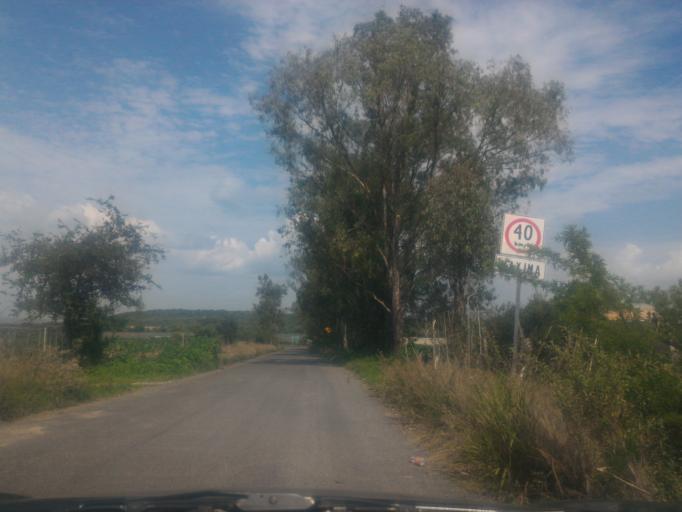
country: MX
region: Guanajuato
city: Ciudad Manuel Doblado
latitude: 20.8351
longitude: -102.0048
